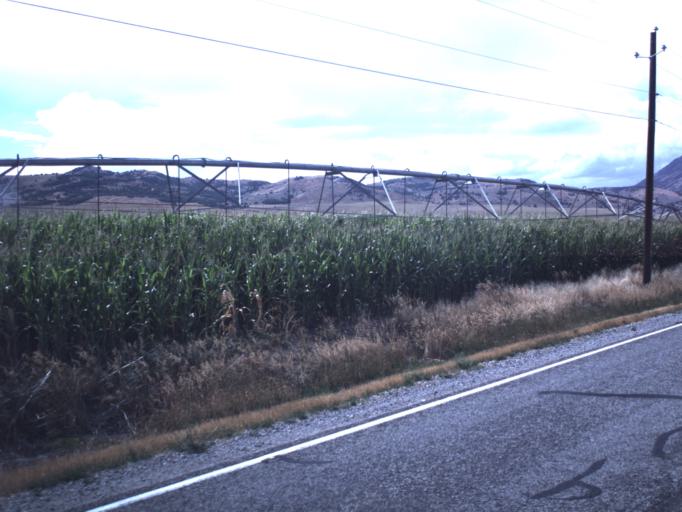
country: US
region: Utah
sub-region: Cache County
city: Benson
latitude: 41.8704
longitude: -112.0136
